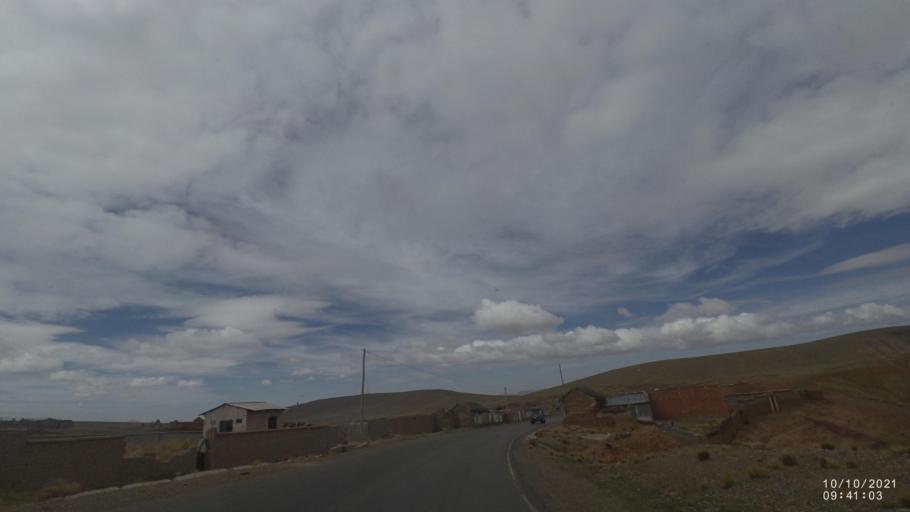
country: BO
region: La Paz
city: Quime
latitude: -17.1440
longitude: -67.3433
